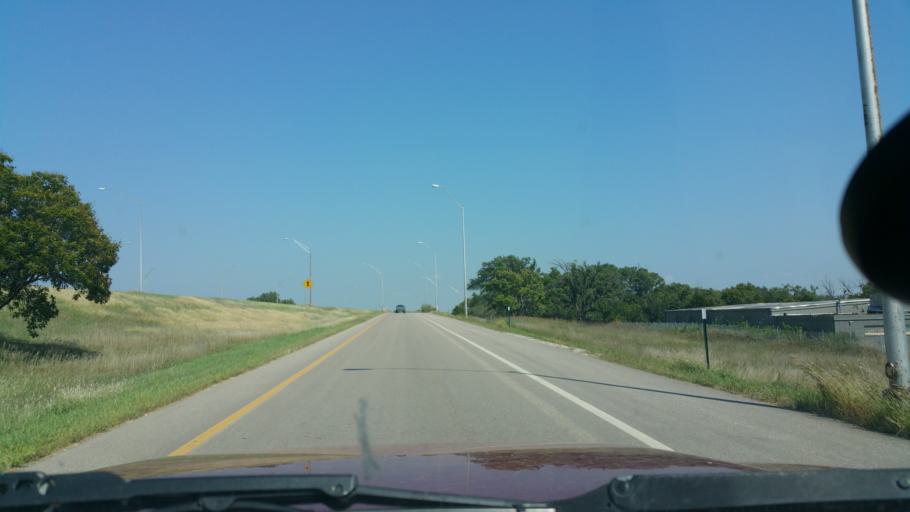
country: US
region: Kansas
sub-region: Dickinson County
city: Abilene
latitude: 38.9397
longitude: -97.2133
